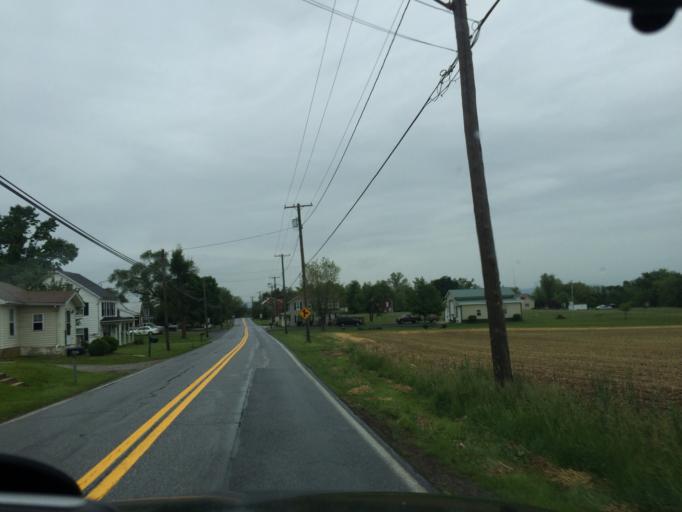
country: US
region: Maryland
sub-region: Carroll County
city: Taneytown
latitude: 39.5945
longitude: -77.2160
